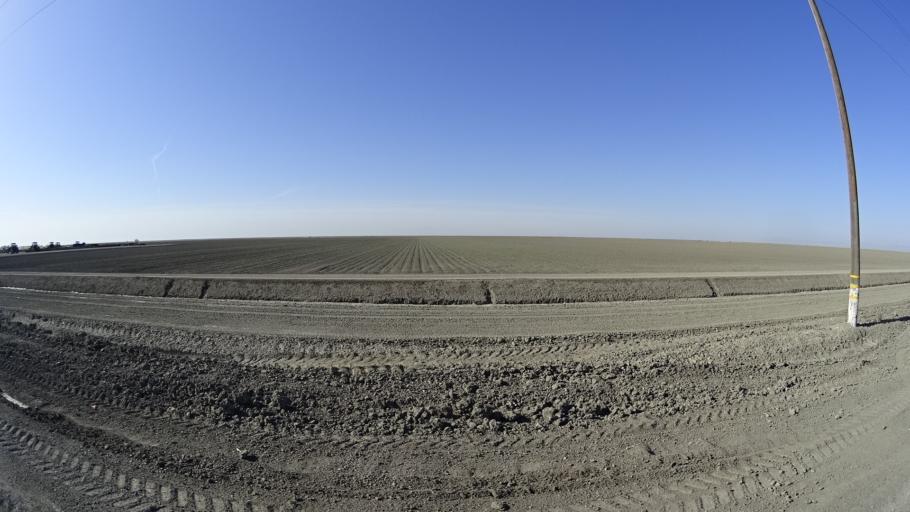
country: US
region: California
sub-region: Kings County
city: Corcoran
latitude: 36.0797
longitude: -119.6838
